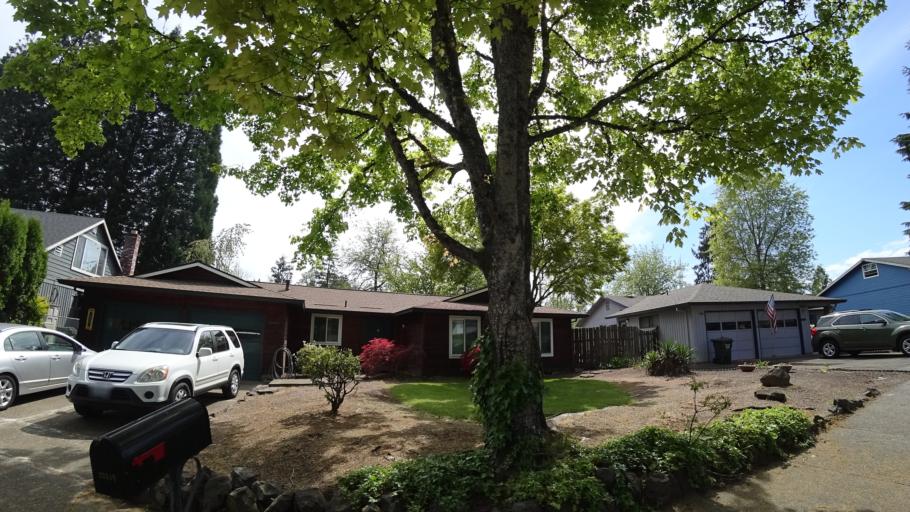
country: US
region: Oregon
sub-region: Washington County
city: Aloha
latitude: 45.4846
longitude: -122.8882
